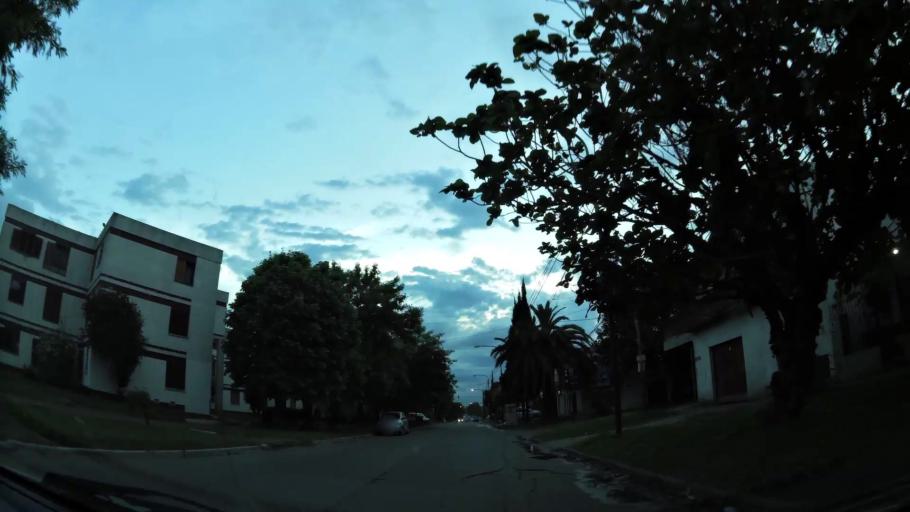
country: AR
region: Buenos Aires
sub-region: Partido de Quilmes
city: Quilmes
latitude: -34.7444
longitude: -58.2472
